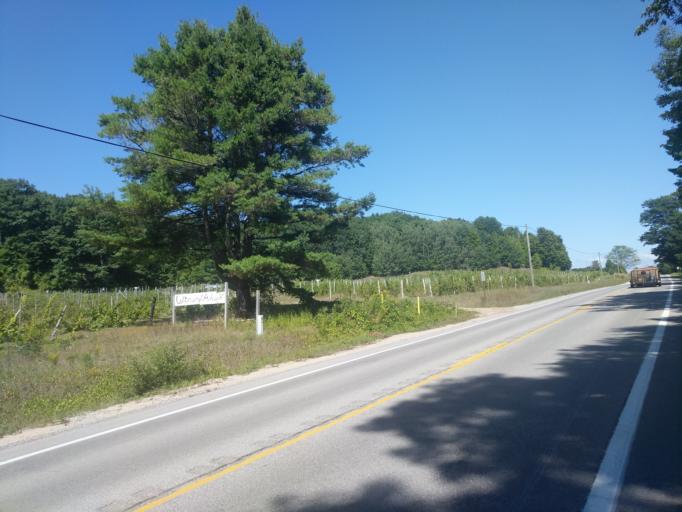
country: US
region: Michigan
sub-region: Leelanau County
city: Leland
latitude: 45.0062
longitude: -85.6250
